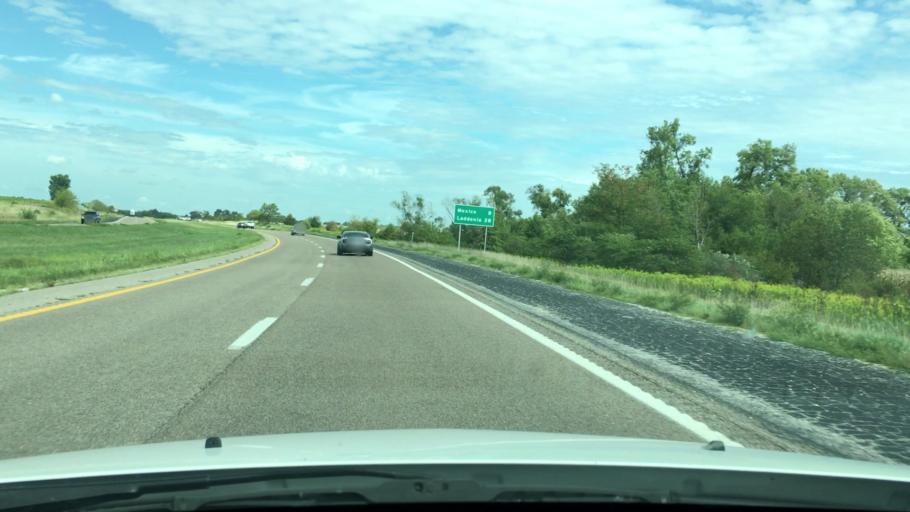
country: US
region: Missouri
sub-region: Audrain County
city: Mexico
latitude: 39.0293
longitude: -91.8857
